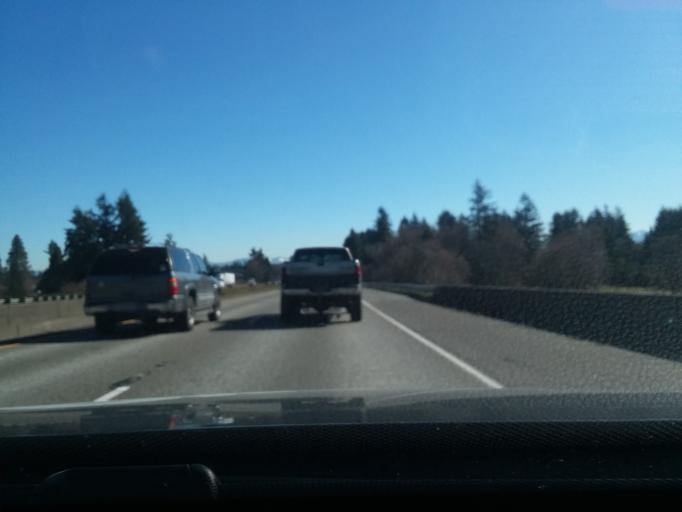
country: US
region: Washington
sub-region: Pierce County
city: Summit
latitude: 47.1582
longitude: -122.3281
